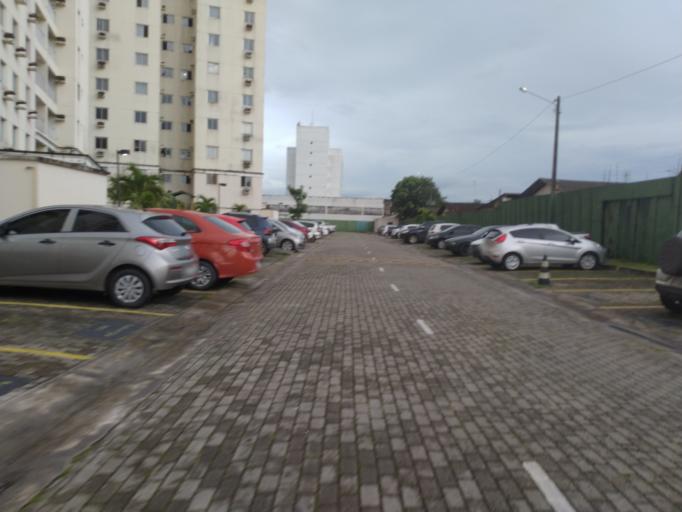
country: BR
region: Para
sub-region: Ananindeua
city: Ananindeua
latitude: -1.3657
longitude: -48.3768
